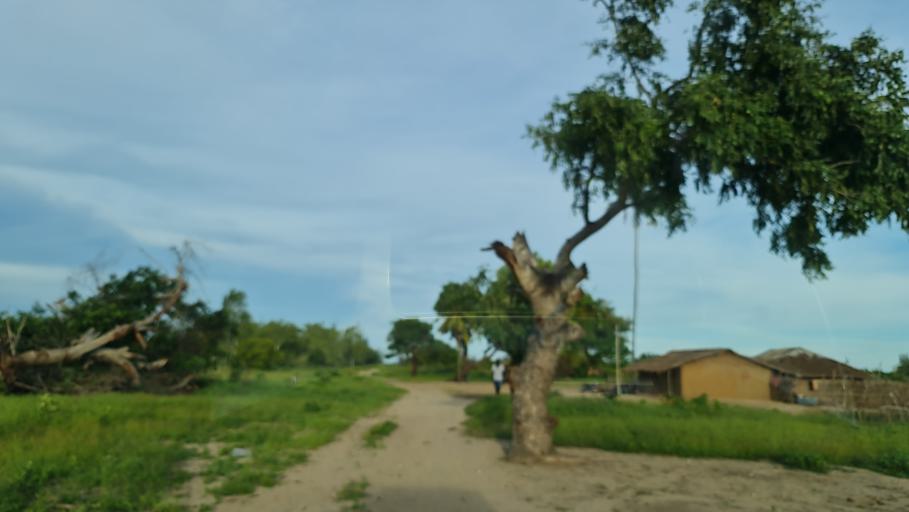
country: MZ
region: Nampula
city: Nacala
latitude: -14.7783
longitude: 40.8186
